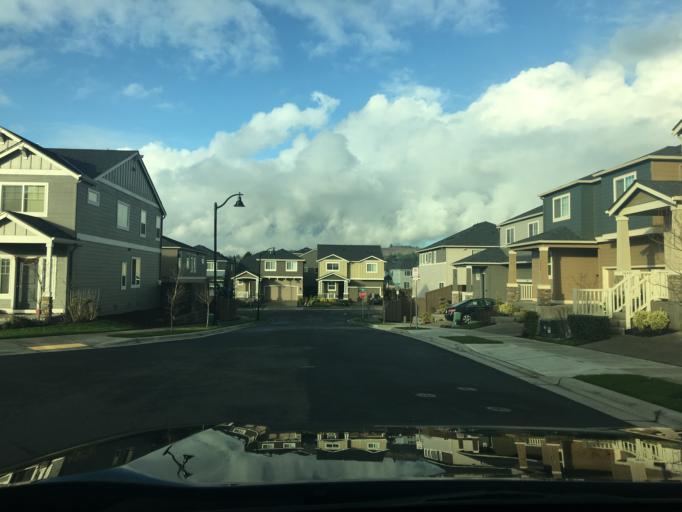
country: US
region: Oregon
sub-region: Washington County
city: Bethany
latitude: 45.5727
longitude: -122.8502
